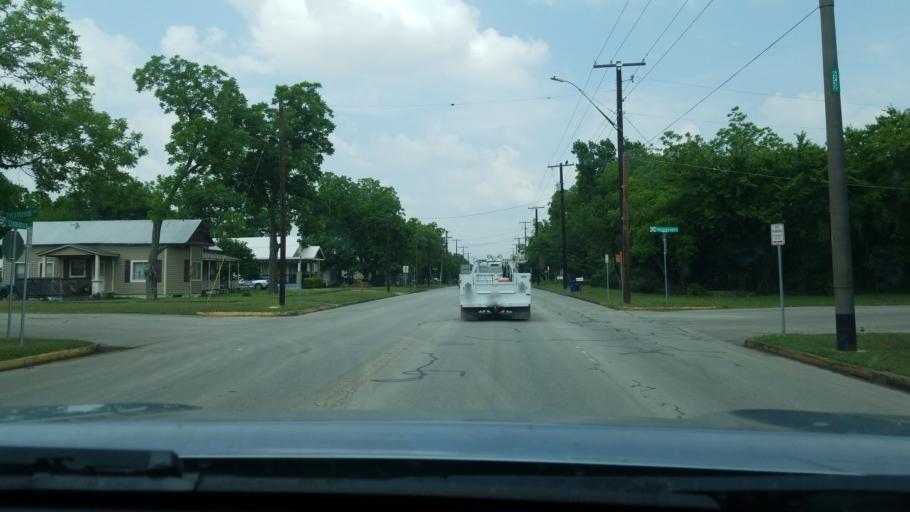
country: US
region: Texas
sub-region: Comal County
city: New Braunfels
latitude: 29.7119
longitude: -98.1159
